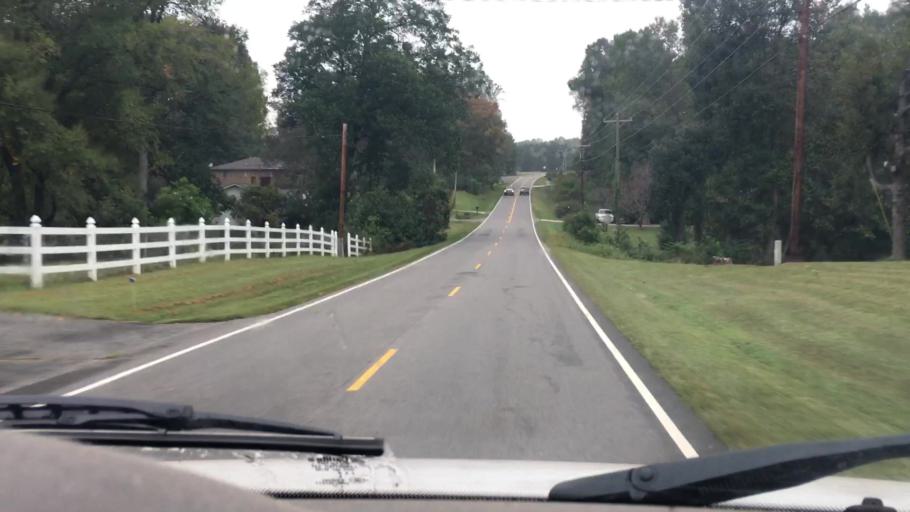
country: US
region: North Carolina
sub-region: Iredell County
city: Mooresville
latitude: 35.6343
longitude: -80.7770
